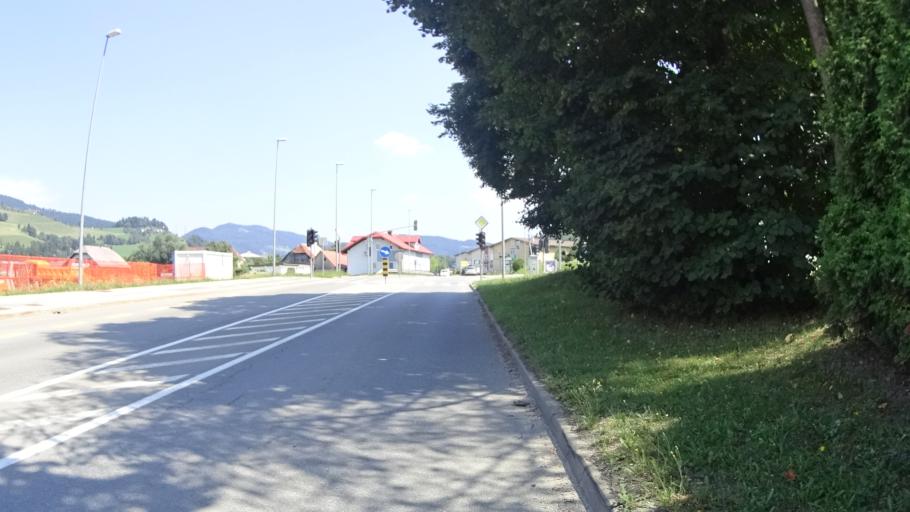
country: SI
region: Prevalje
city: Prevalje
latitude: 46.5444
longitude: 14.9431
